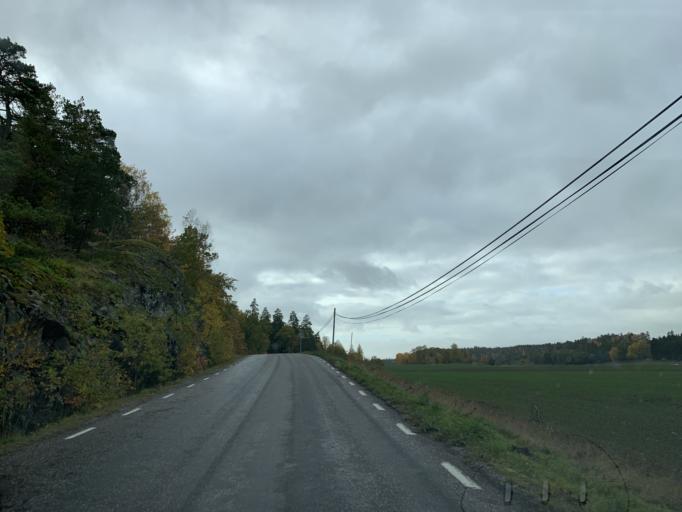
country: SE
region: Stockholm
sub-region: Nynashamns Kommun
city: Osmo
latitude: 58.9506
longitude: 17.7659
